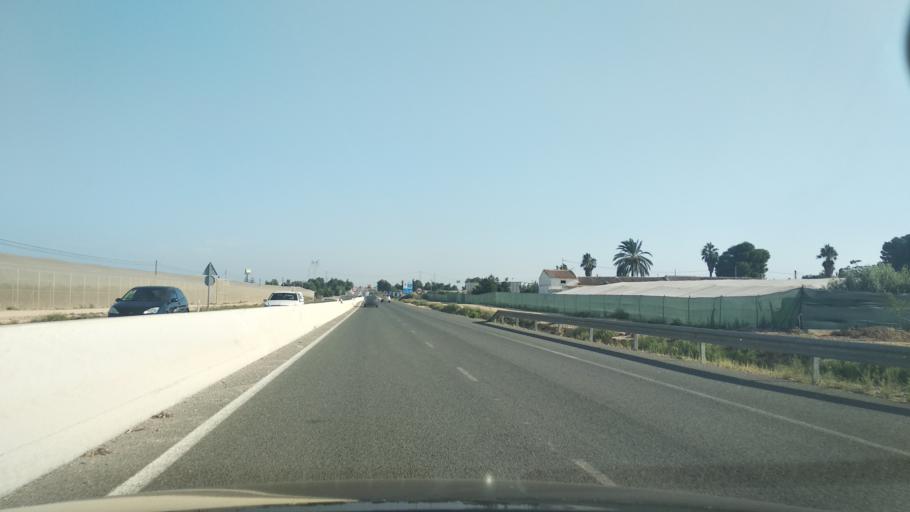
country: ES
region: Murcia
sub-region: Murcia
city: San Javier
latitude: 37.8200
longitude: -0.8478
